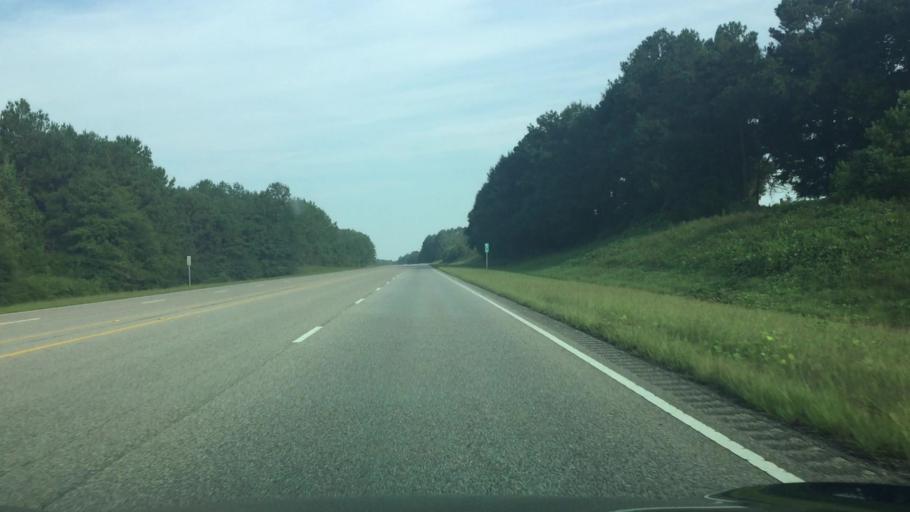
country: US
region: Alabama
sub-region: Covington County
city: Andalusia
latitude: 31.4004
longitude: -86.5839
